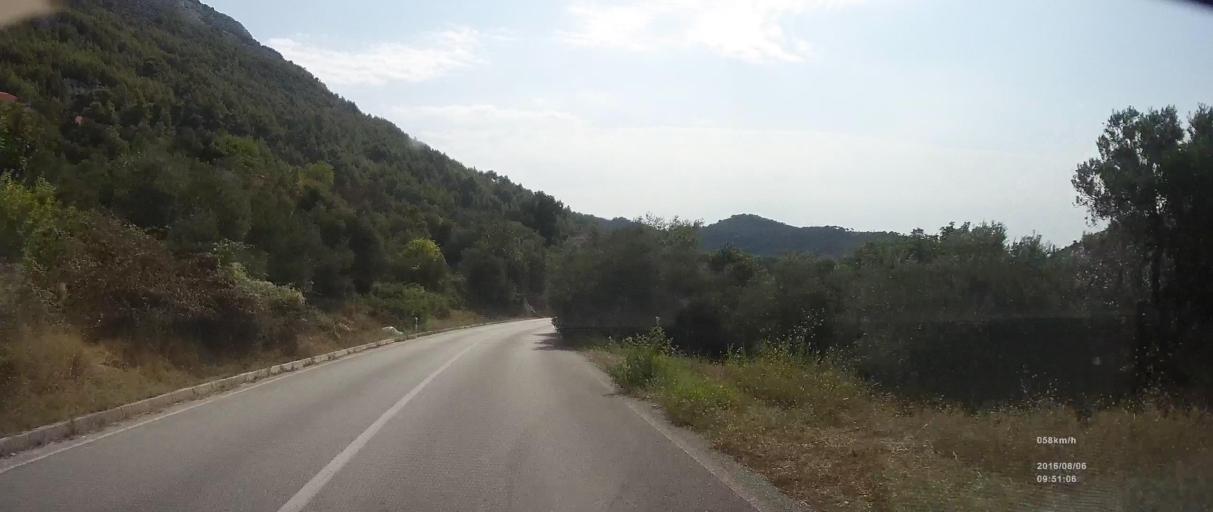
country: HR
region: Dubrovacko-Neretvanska
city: Blato
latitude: 42.7320
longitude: 17.5606
